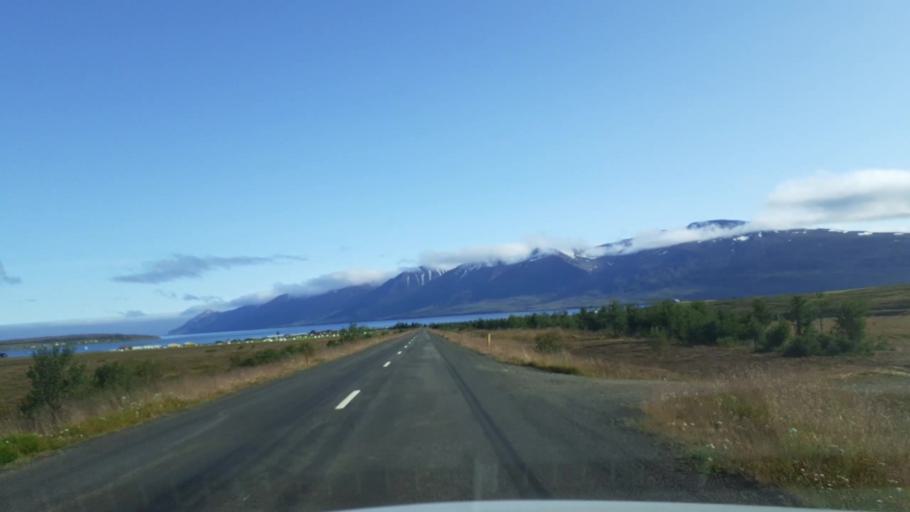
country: IS
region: Northeast
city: Dalvik
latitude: 65.9332
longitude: -18.3593
